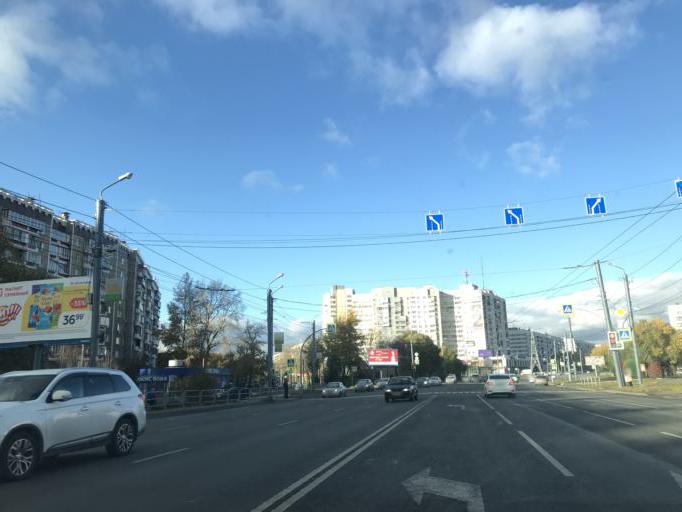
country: RU
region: Chelyabinsk
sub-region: Gorod Chelyabinsk
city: Chelyabinsk
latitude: 55.1696
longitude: 61.4530
